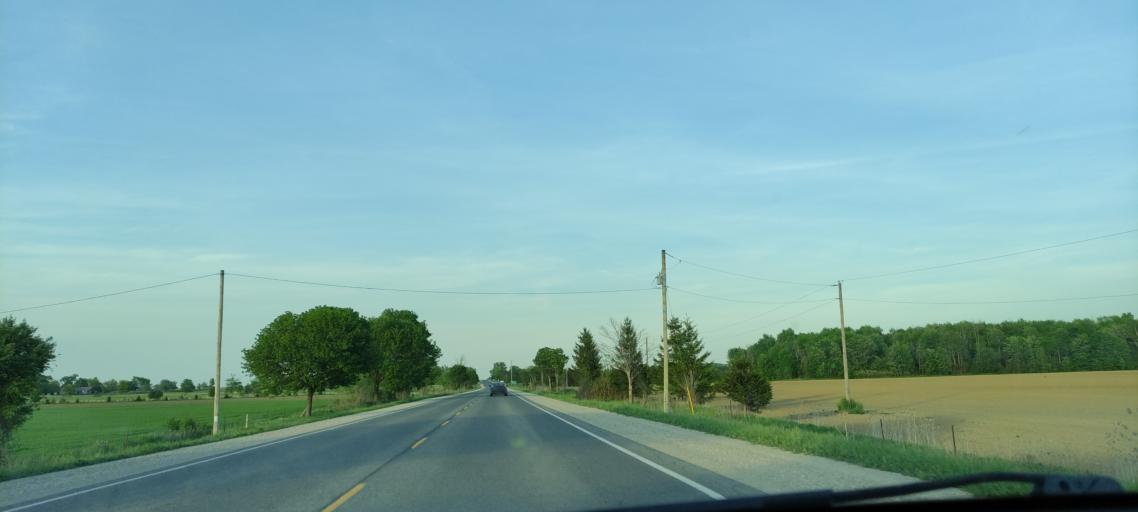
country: CA
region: Ontario
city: London
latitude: 43.1956
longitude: -81.2513
